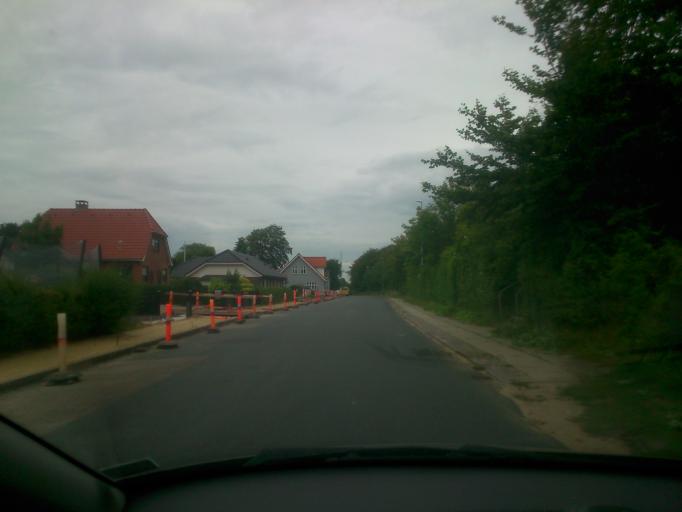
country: DK
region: South Denmark
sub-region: Esbjerg Kommune
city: Esbjerg
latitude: 55.5331
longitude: 8.4414
